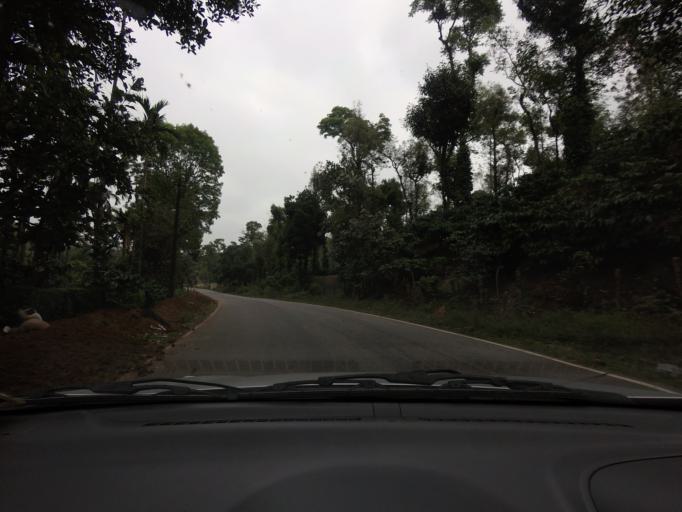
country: IN
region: Karnataka
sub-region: Hassan
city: Sakleshpur
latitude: 12.9496
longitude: 75.7496
